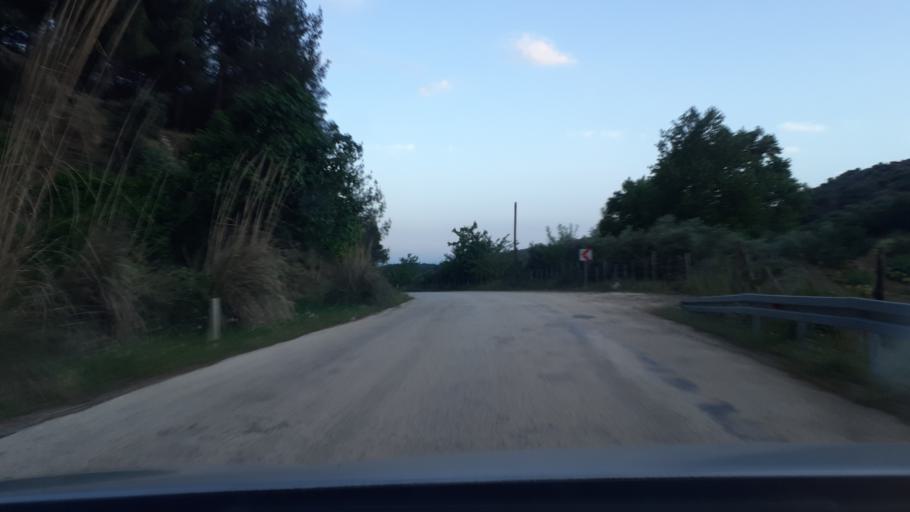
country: TR
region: Hatay
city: Kirikhan
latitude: 36.5195
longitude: 36.3182
